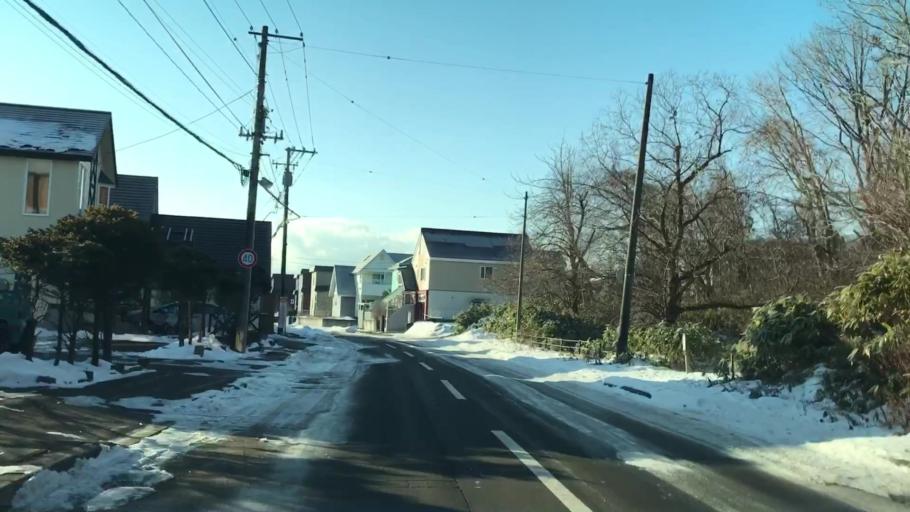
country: JP
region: Hokkaido
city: Muroran
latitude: 42.3875
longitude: 141.0652
